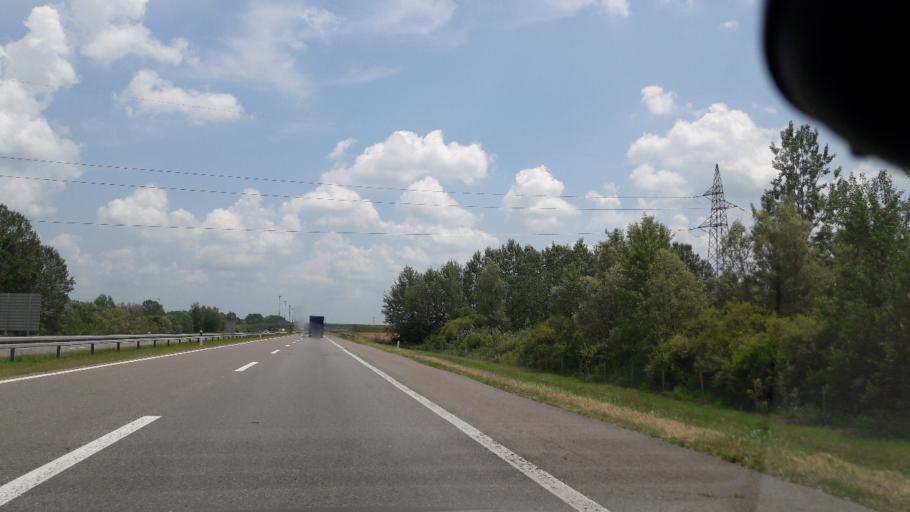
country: HR
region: Vukovarsko-Srijemska
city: Zupanja
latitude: 45.1043
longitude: 18.7074
